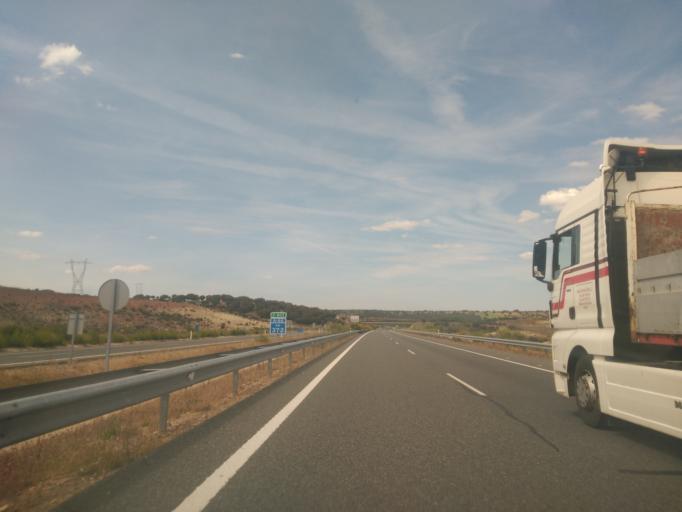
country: ES
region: Castille and Leon
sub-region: Provincia de Salamanca
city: Belena
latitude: 40.7016
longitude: -5.6248
